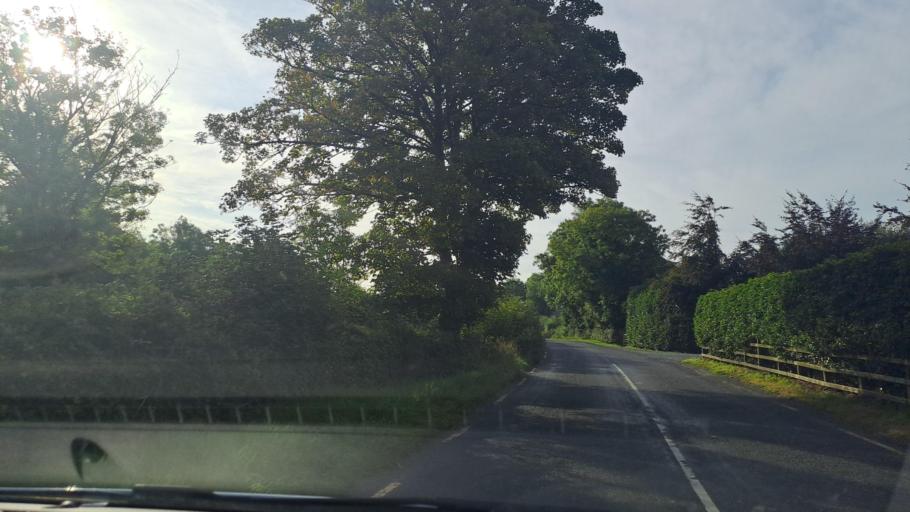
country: IE
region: Ulster
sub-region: An Cabhan
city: Kingscourt
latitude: 53.9321
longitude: -6.8178
